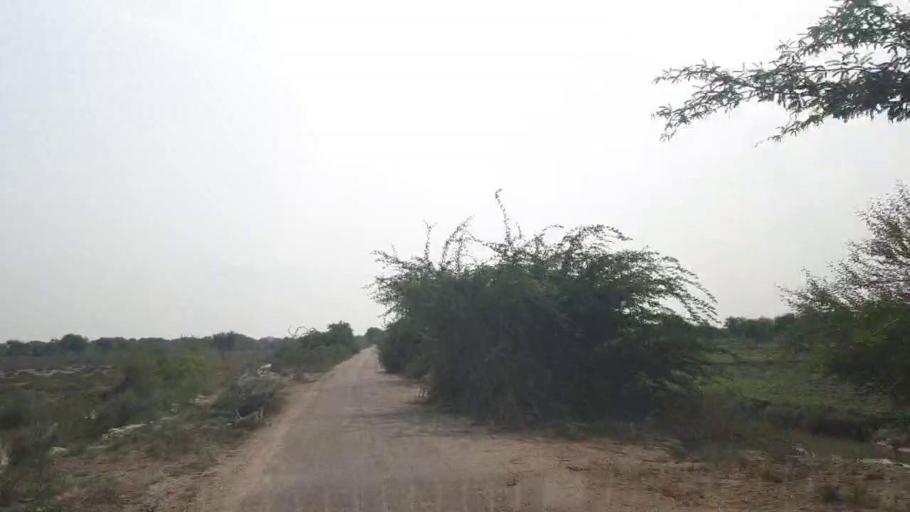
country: PK
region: Sindh
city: Badin
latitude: 24.5502
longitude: 68.6877
